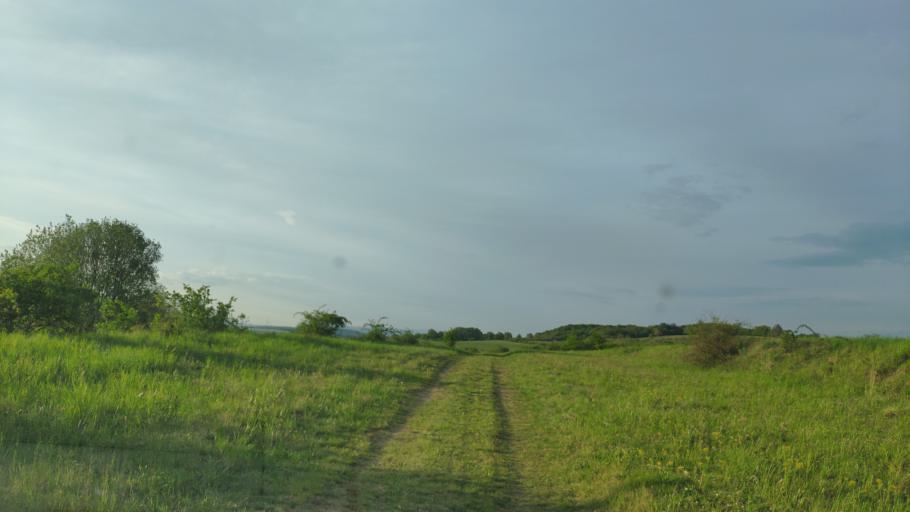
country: SK
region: Kosicky
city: Kosice
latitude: 48.7165
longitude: 21.3545
